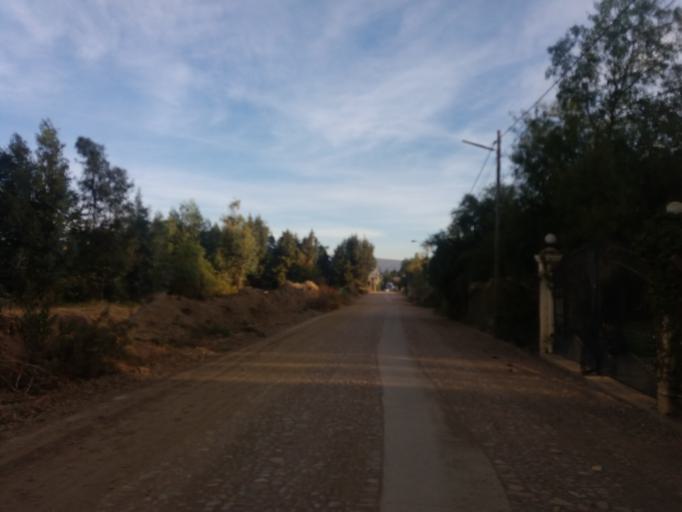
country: BO
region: Cochabamba
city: Cochabamba
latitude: -17.3495
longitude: -66.2185
